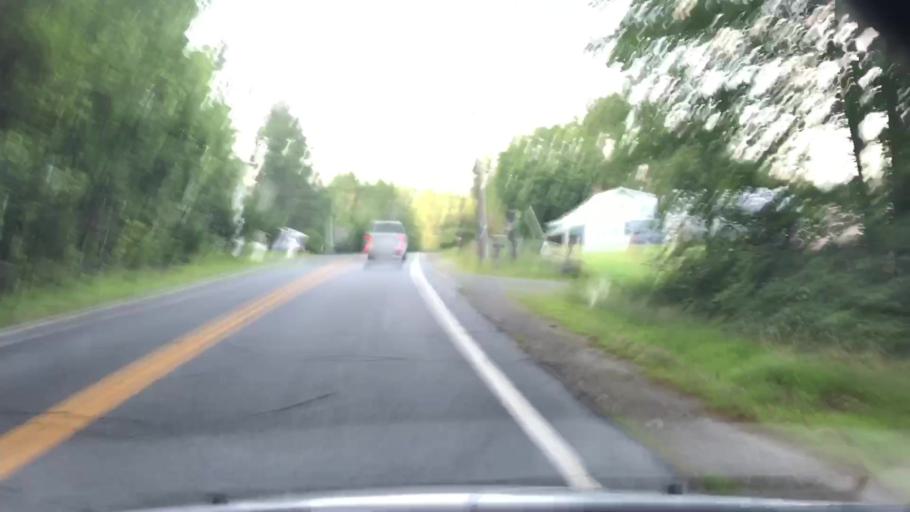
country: US
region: New Hampshire
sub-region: Grafton County
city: Rumney
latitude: 43.8764
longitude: -71.9122
